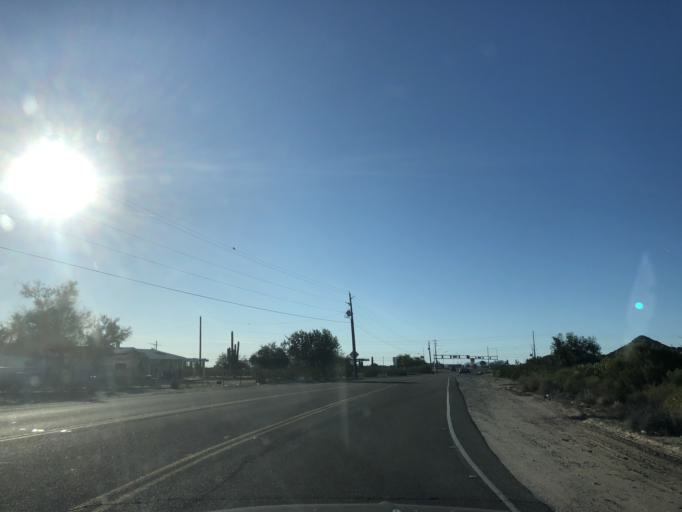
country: US
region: Arizona
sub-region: Maricopa County
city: Buckeye
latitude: 33.4283
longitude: -112.5873
